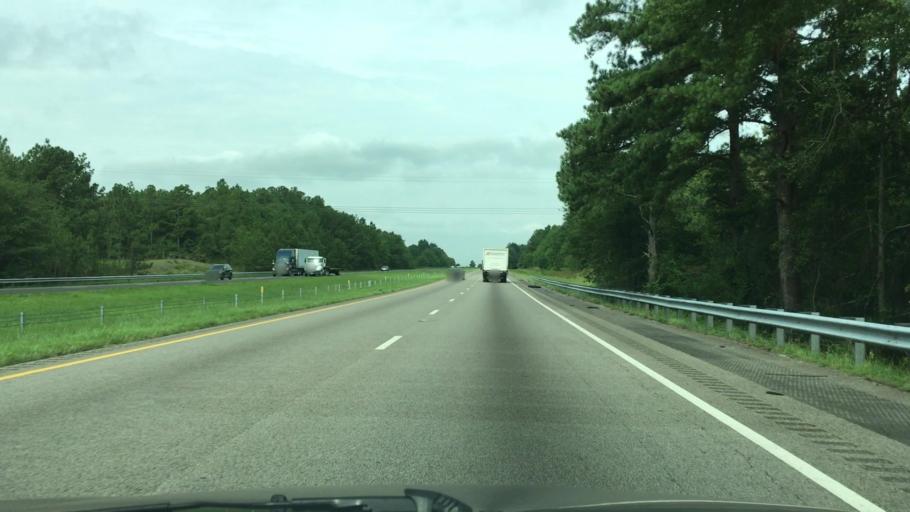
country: US
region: South Carolina
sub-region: Aiken County
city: Graniteville
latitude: 33.6345
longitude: -81.7748
